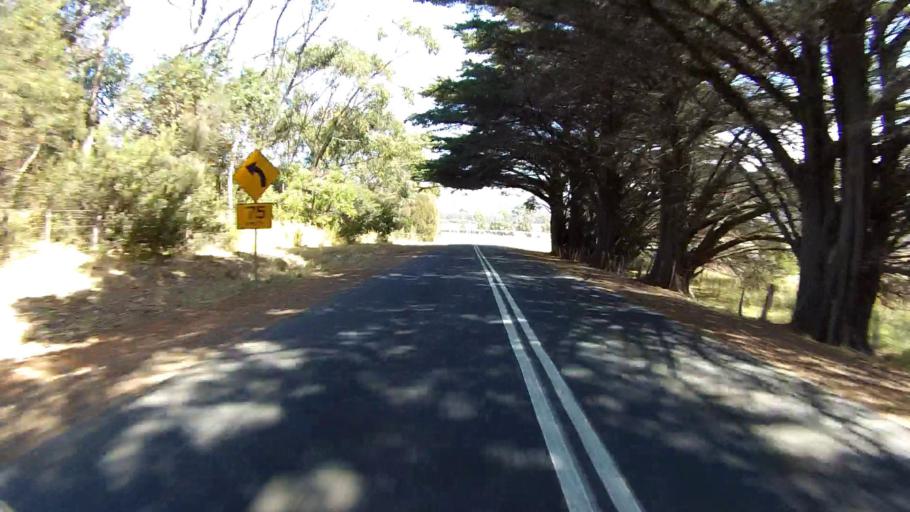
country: AU
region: Tasmania
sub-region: Sorell
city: Sorell
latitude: -42.2001
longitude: 148.0462
